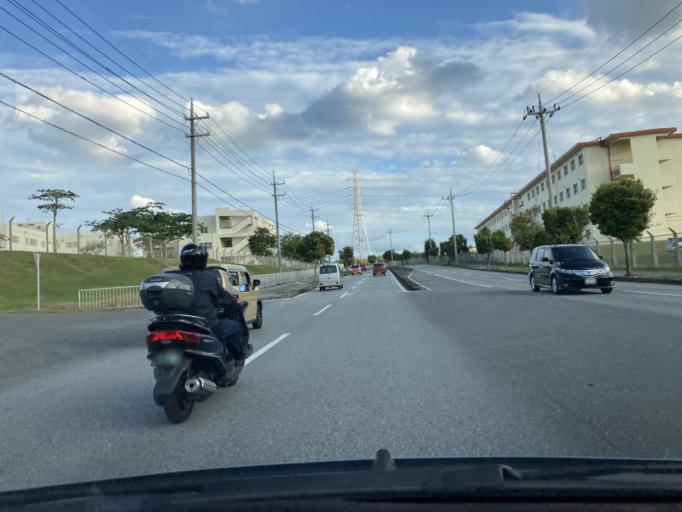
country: JP
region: Okinawa
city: Chatan
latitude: 26.3069
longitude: 127.7706
